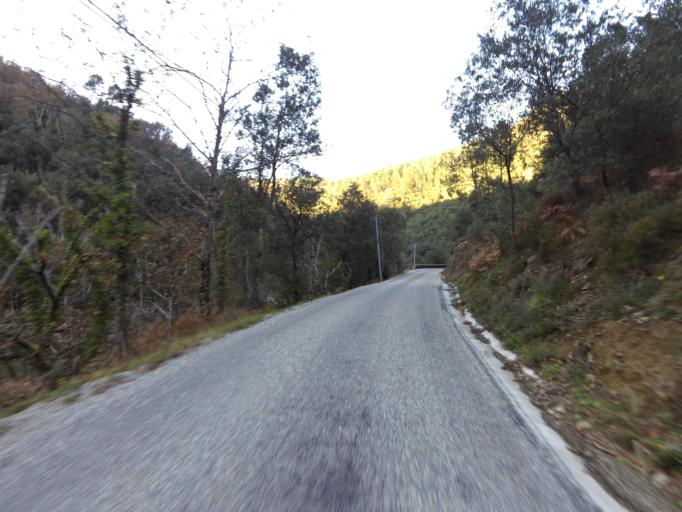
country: FR
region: Rhone-Alpes
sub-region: Departement de l'Ardeche
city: Lablachere
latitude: 44.5169
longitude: 4.1890
